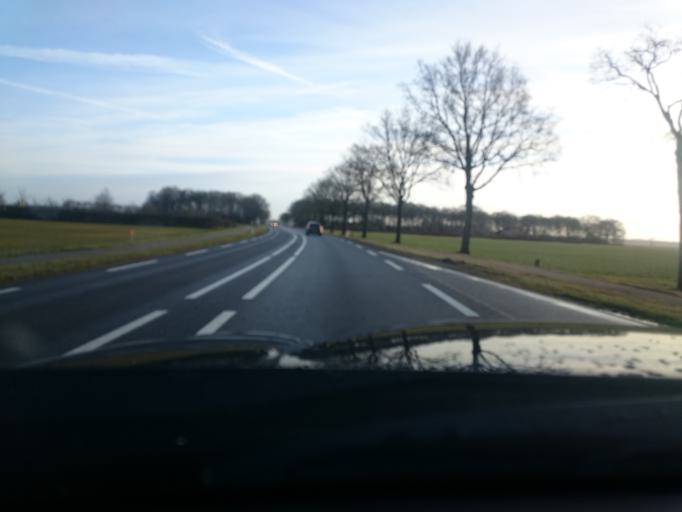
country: NL
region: Overijssel
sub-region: Gemeente Raalte
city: Raalte
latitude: 52.3504
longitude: 6.2344
